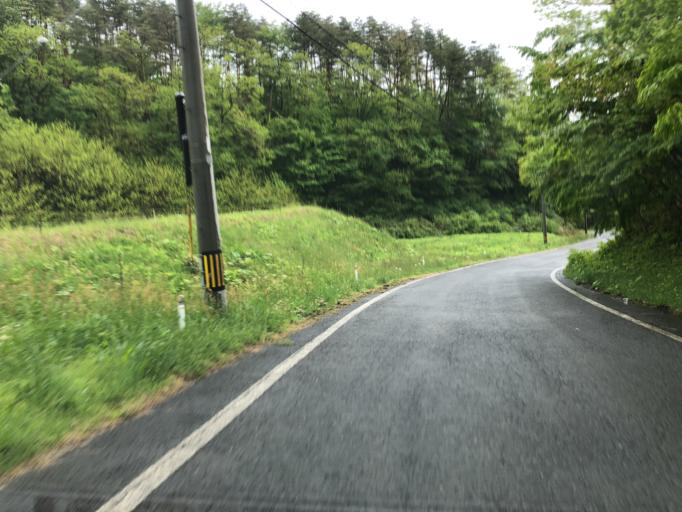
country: JP
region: Fukushima
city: Ishikawa
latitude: 37.0303
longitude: 140.5550
